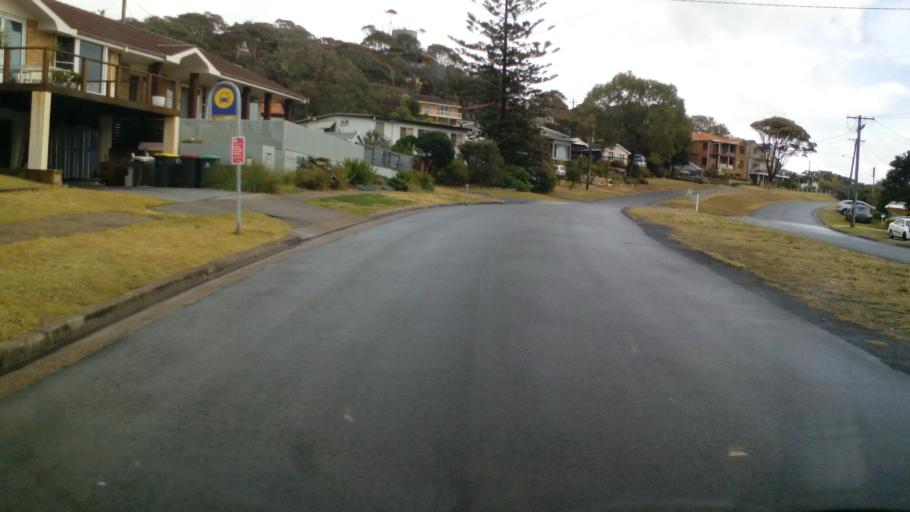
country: AU
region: New South Wales
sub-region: Lake Macquarie Shire
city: Belmont South
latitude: -33.1101
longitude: 151.6428
